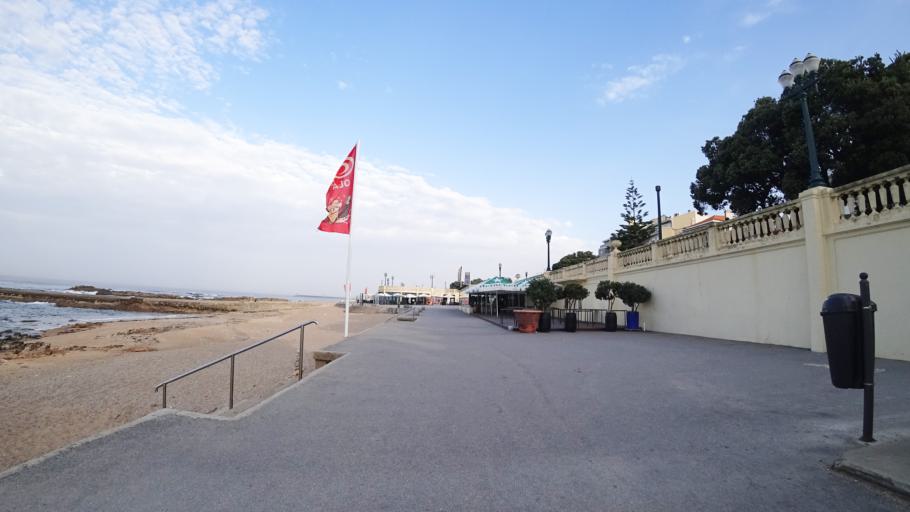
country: PT
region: Porto
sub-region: Matosinhos
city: Matosinhos
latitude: 41.1580
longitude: -8.6833
